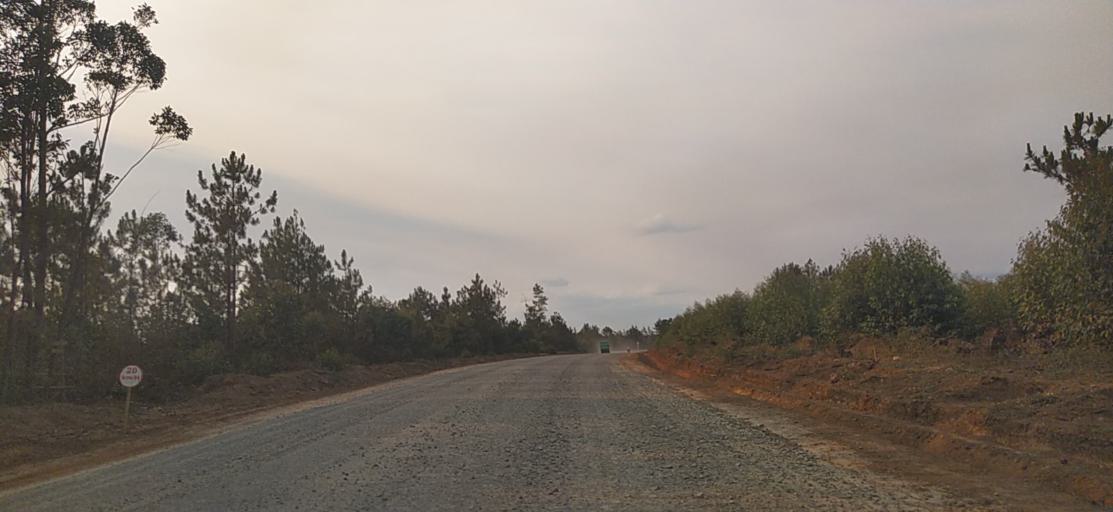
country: MG
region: Alaotra Mangoro
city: Moramanga
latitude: -18.5582
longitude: 48.2590
